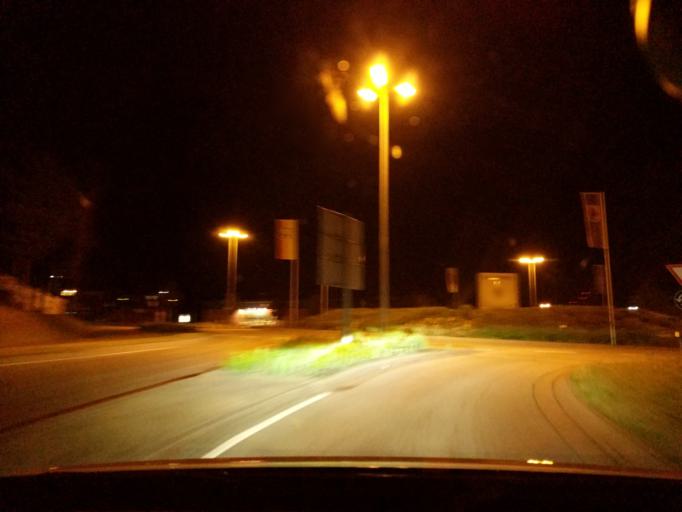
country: DE
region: Rheinland-Pfalz
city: Weilerbach
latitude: 49.4764
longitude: 7.6392
